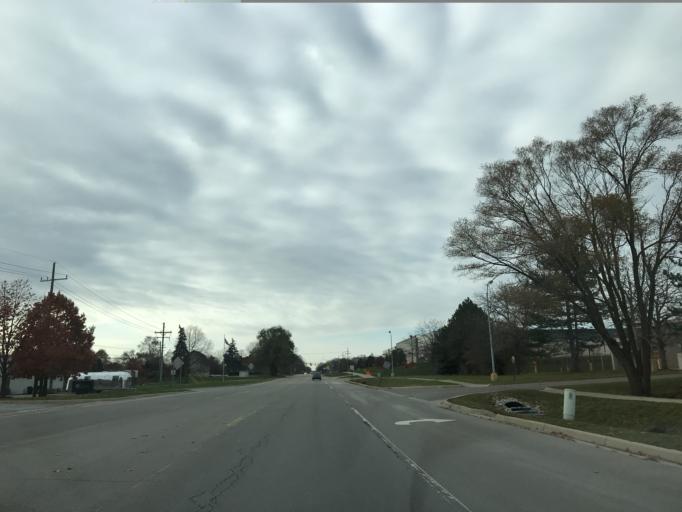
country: US
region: Michigan
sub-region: Washtenaw County
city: Ann Arbor
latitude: 42.2294
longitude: -83.7404
